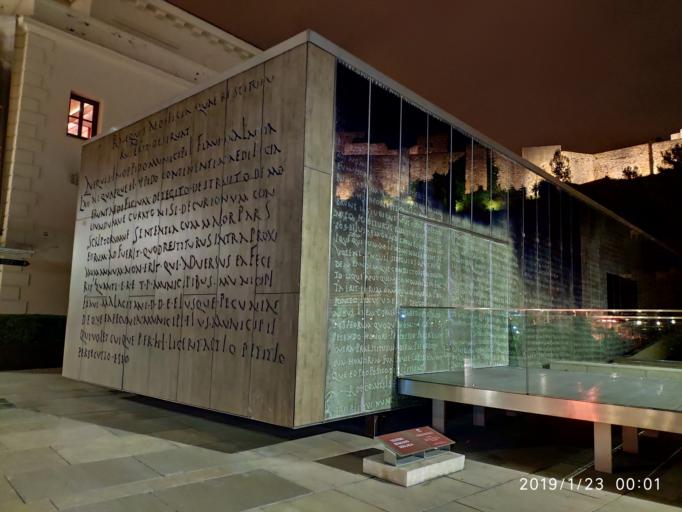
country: ES
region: Andalusia
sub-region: Provincia de Malaga
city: Malaga
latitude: 36.7216
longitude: -4.4171
